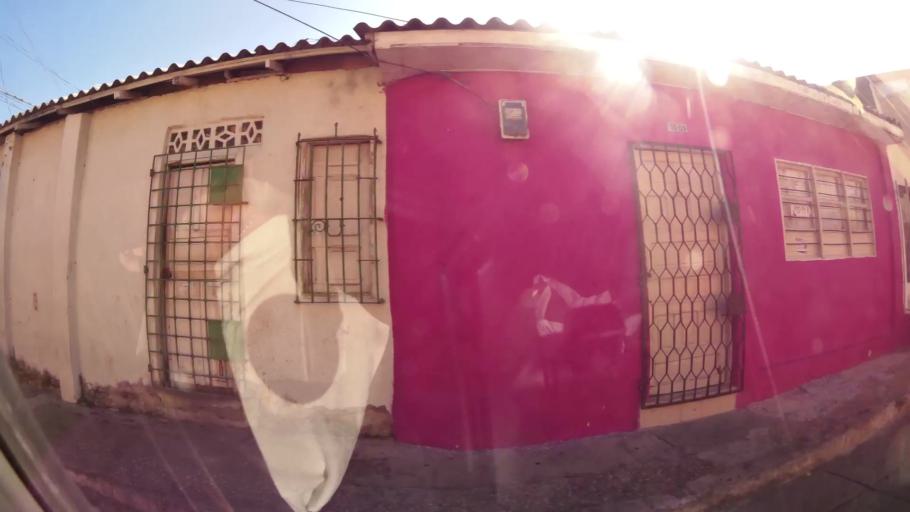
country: CO
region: Atlantico
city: Barranquilla
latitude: 10.9714
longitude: -74.7823
